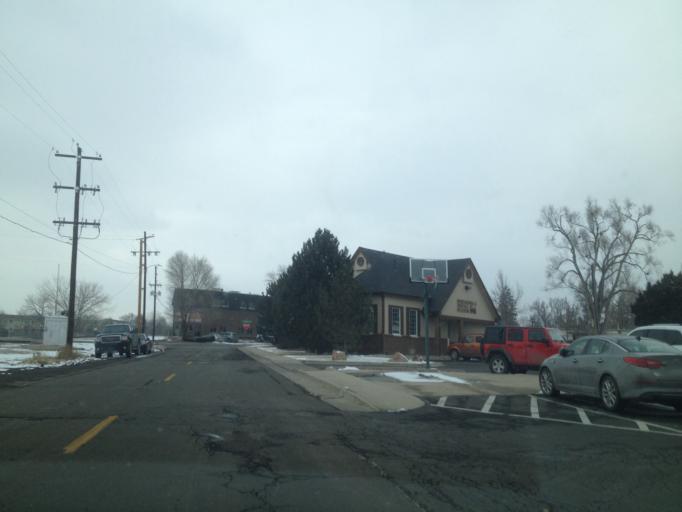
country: US
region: Colorado
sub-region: Adams County
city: Westminster
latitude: 39.8282
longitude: -105.0397
